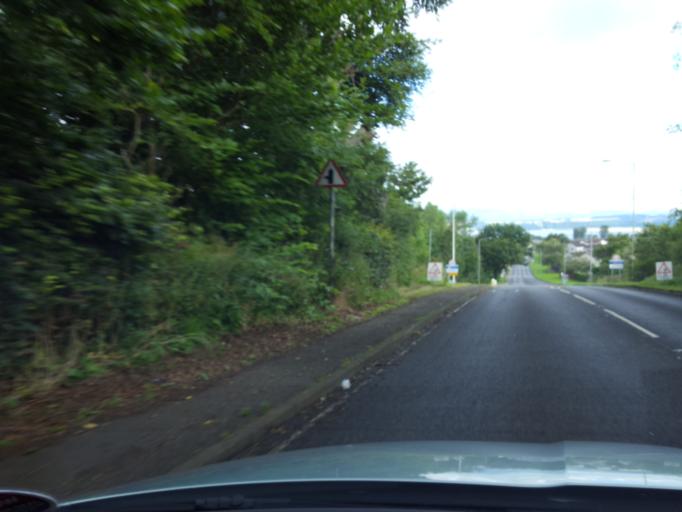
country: GB
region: Scotland
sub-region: Falkirk
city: Bo'ness
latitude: 56.0018
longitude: -3.6090
